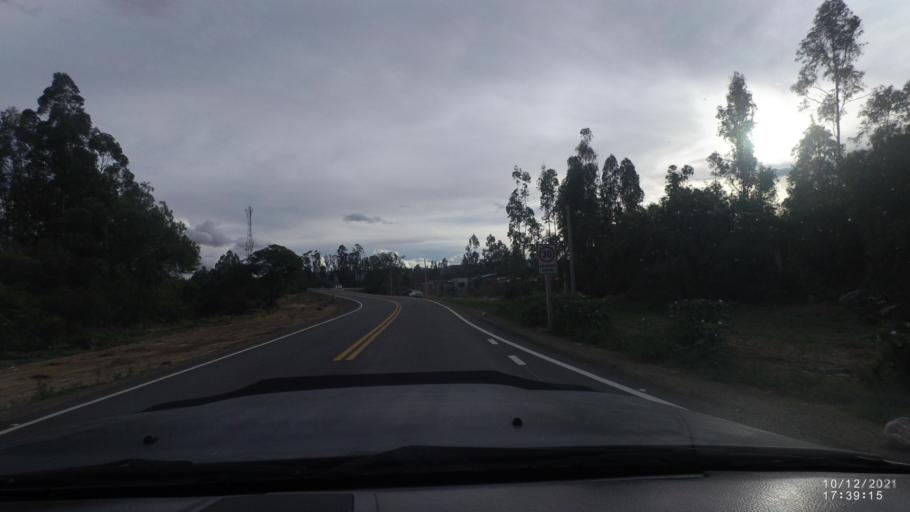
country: BO
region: Cochabamba
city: Tarata
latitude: -17.5773
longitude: -66.0137
